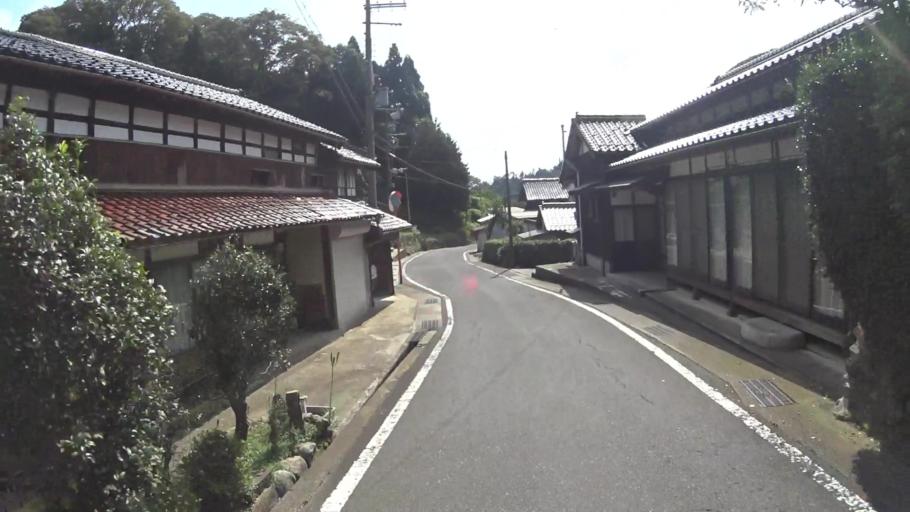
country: JP
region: Kyoto
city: Miyazu
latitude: 35.6711
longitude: 135.2443
